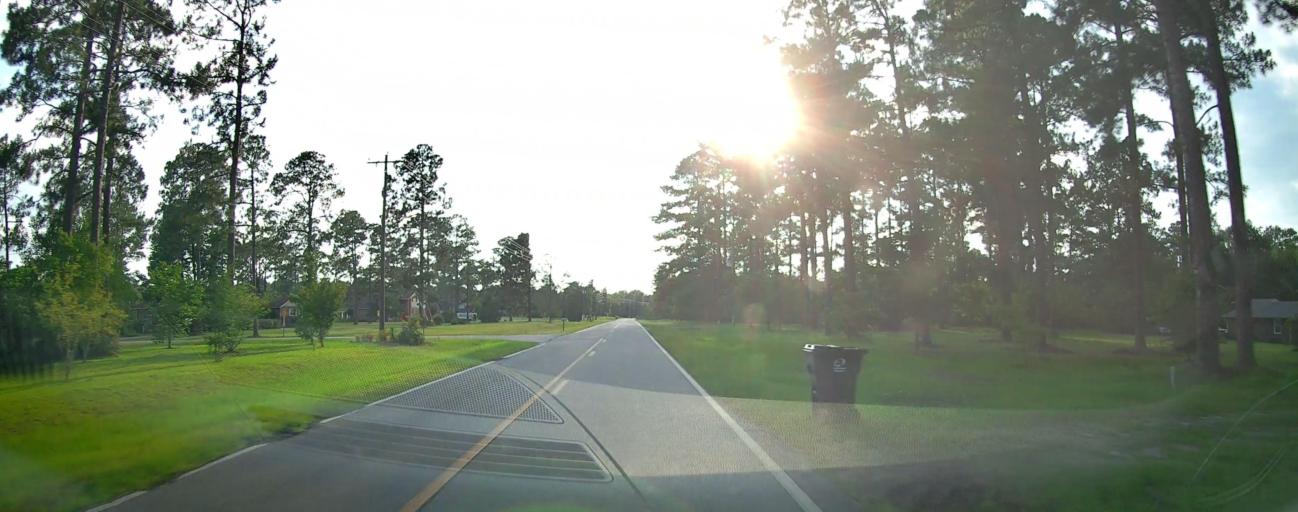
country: US
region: Georgia
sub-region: Peach County
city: Byron
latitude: 32.7042
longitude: -83.8208
